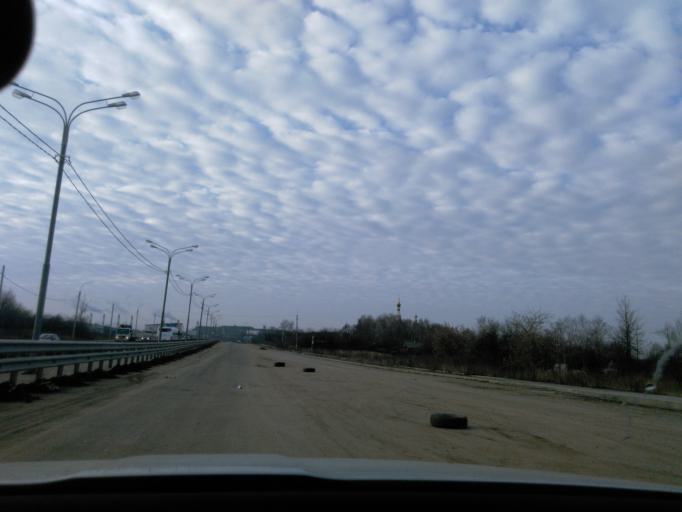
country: RU
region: Moskovskaya
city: Dolgoprudnyy
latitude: 55.9217
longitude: 37.4932
